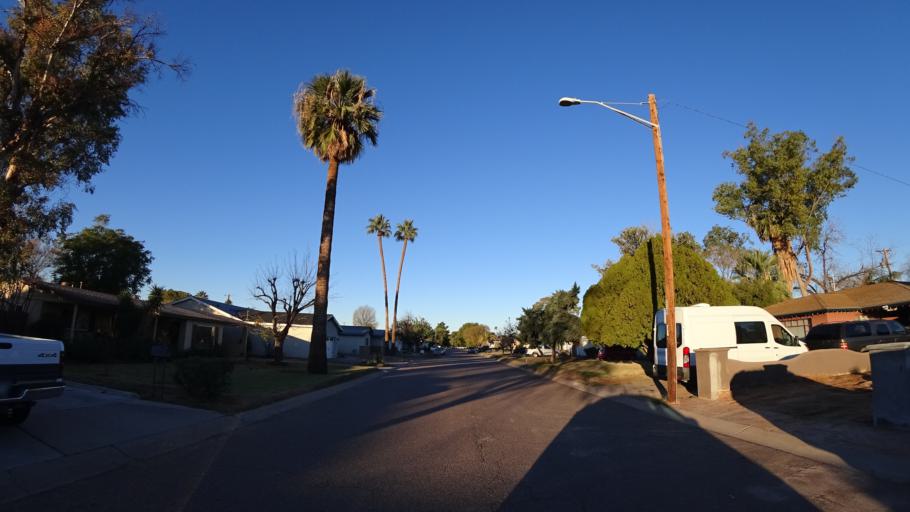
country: US
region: Arizona
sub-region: Maricopa County
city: Paradise Valley
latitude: 33.4853
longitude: -111.9880
